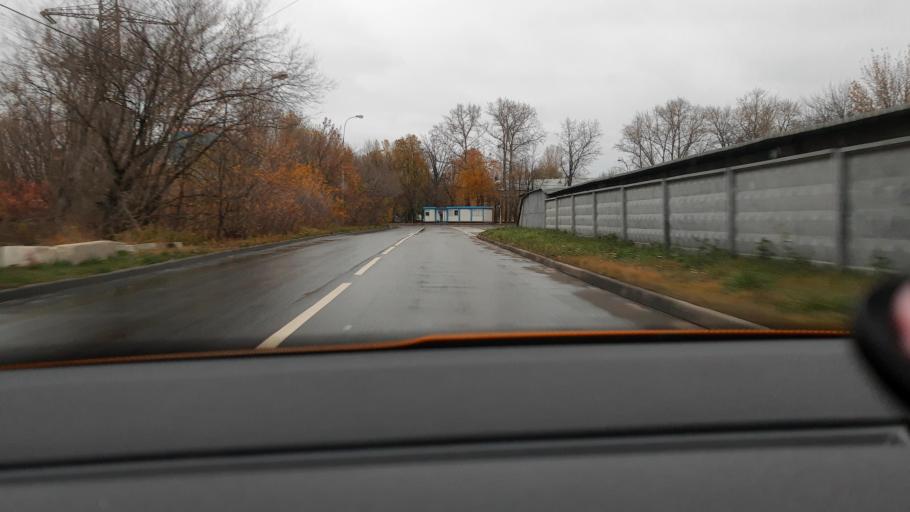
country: RU
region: Moscow
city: Businovo
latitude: 55.8929
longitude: 37.5142
